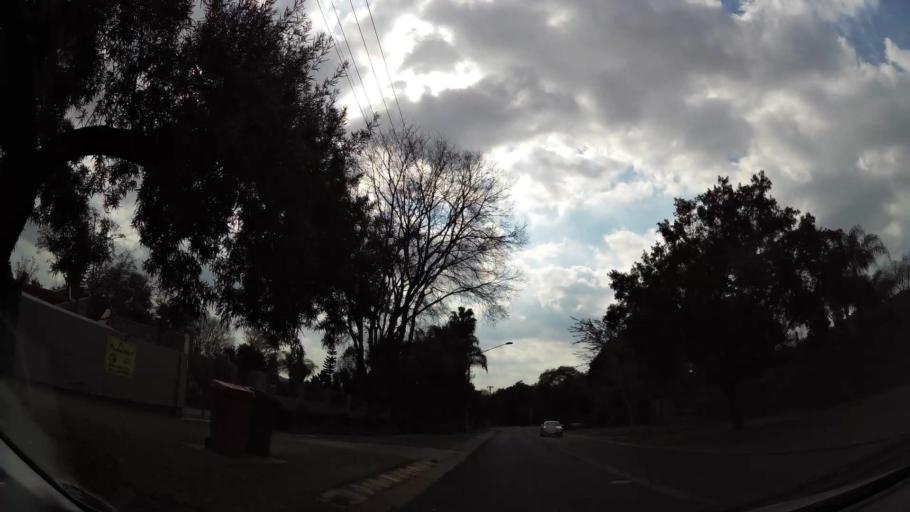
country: ZA
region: Gauteng
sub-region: City of Tshwane Metropolitan Municipality
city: Pretoria
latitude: -25.7572
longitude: 28.2940
